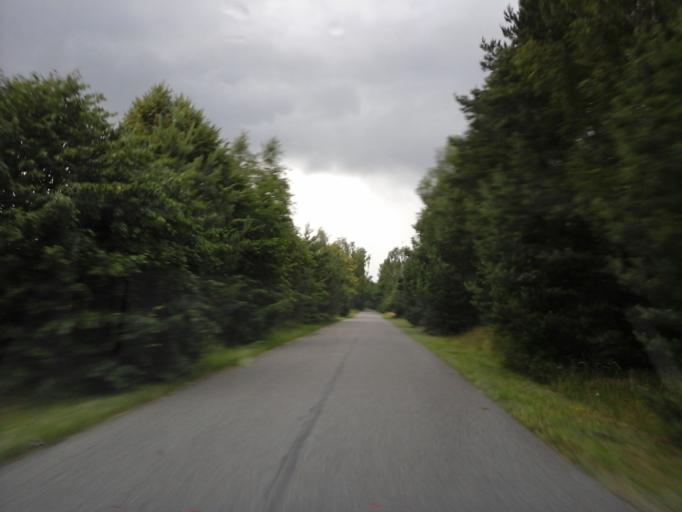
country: PL
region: West Pomeranian Voivodeship
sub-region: Powiat choszczenski
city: Bierzwnik
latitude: 53.0448
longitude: 15.6333
